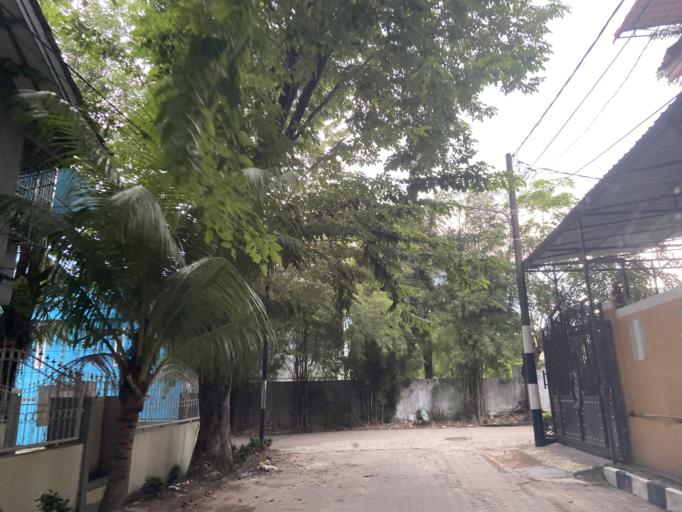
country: SG
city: Singapore
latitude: 1.1227
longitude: 104.0225
